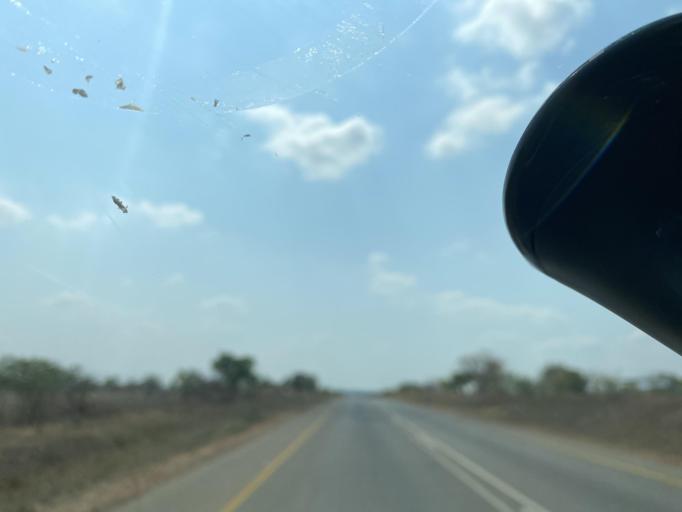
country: ZM
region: Lusaka
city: Chongwe
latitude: -15.5502
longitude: 28.6751
